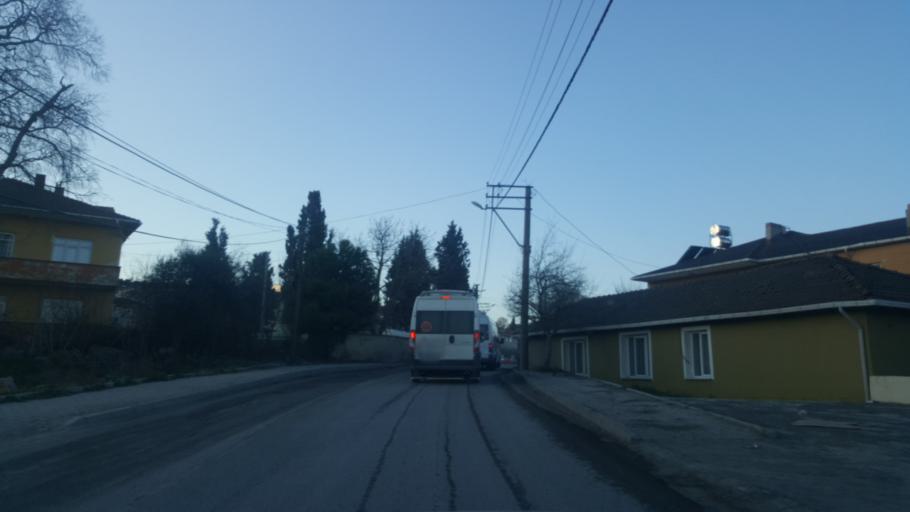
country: TR
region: Kocaeli
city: Tavsanli
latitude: 40.8482
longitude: 29.5550
